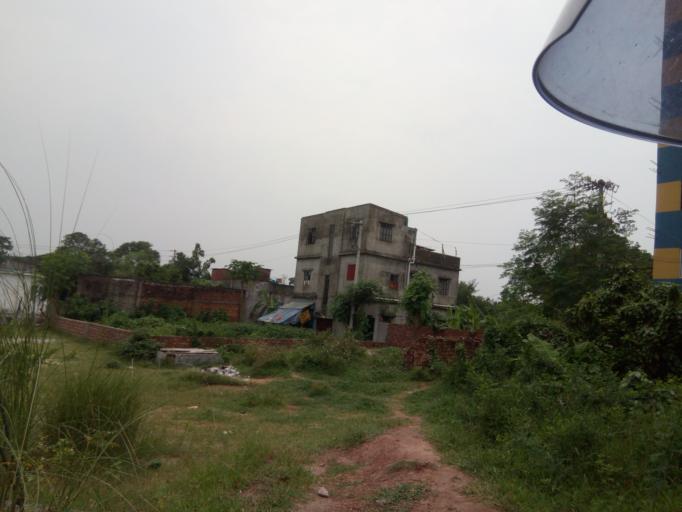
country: BD
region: Dhaka
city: Azimpur
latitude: 23.7394
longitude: 90.3366
